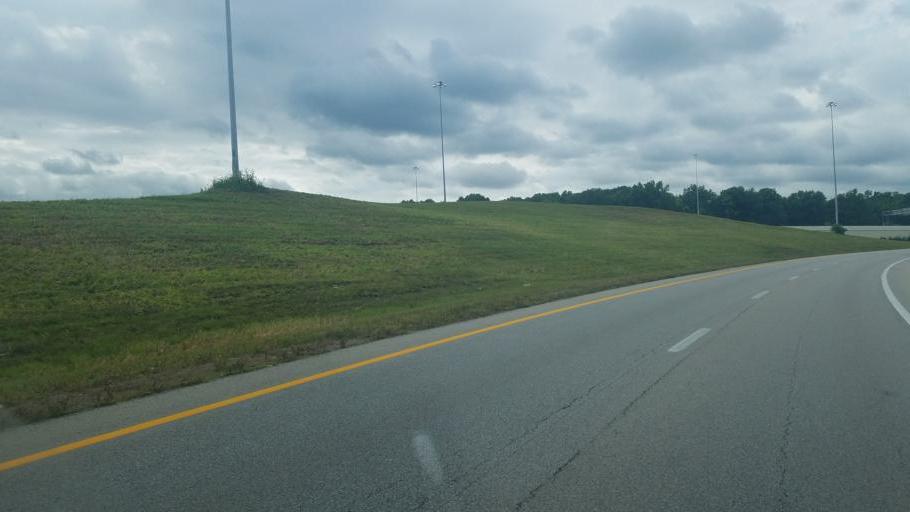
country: US
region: Ohio
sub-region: Franklin County
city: Huber Ridge
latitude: 40.0832
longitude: -82.9051
